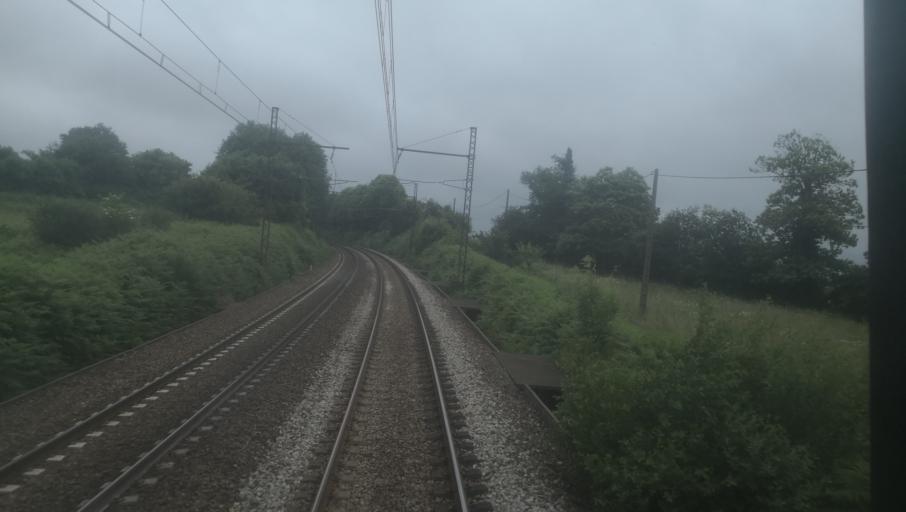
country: FR
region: Limousin
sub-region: Departement de la Creuse
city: Saint-Agnant-de-Versillat
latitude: 46.2864
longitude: 1.4815
